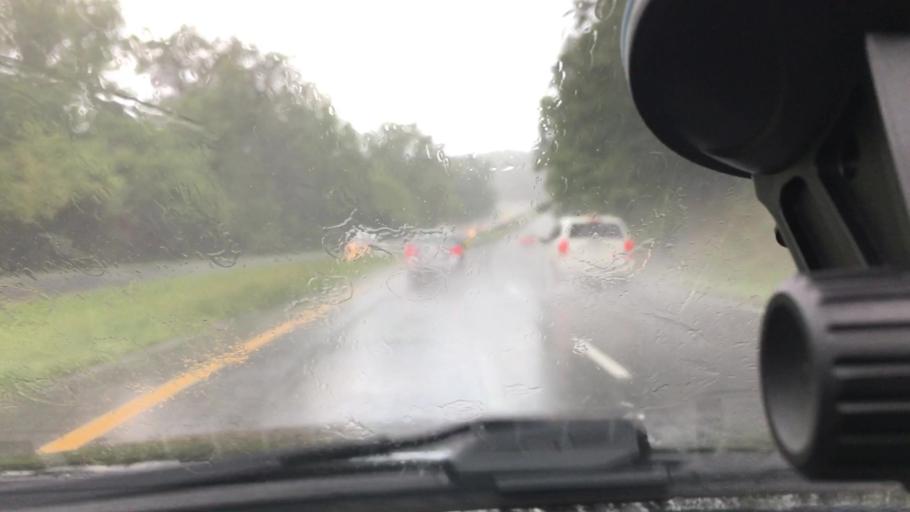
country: US
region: North Carolina
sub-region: Cleveland County
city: White Plains
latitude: 35.2584
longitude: -81.4601
